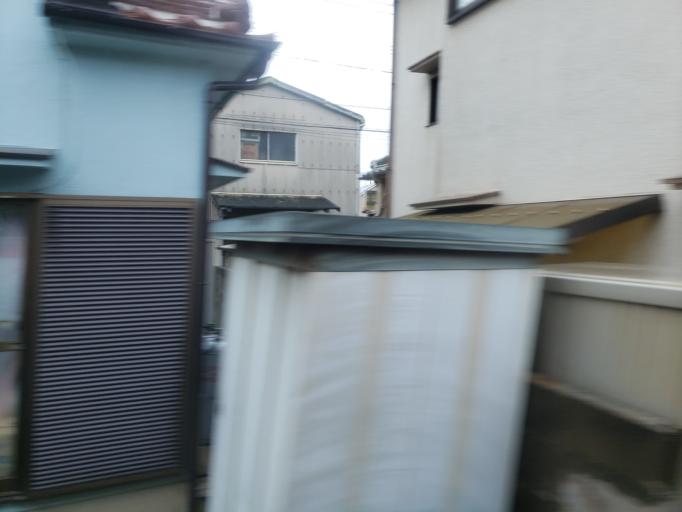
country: JP
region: Hyogo
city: Kakogawacho-honmachi
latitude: 34.7132
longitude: 134.8712
